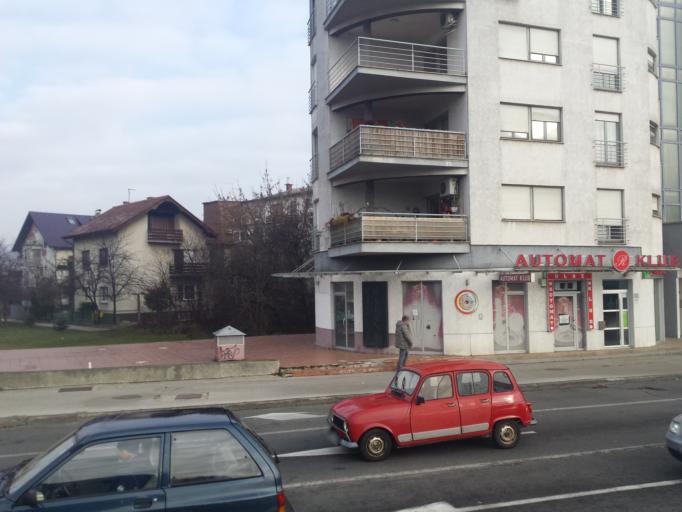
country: HR
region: Grad Zagreb
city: Jankomir
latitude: 45.7891
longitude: 15.9232
